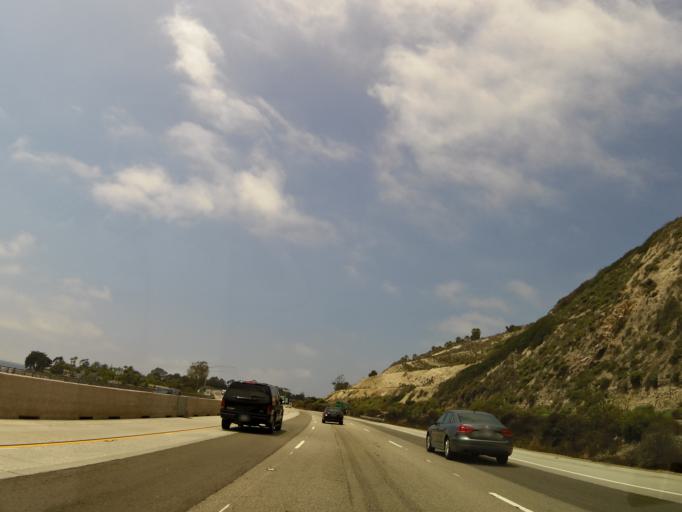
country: US
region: California
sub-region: Santa Barbara County
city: Carpinteria
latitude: 34.3765
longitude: -119.4699
